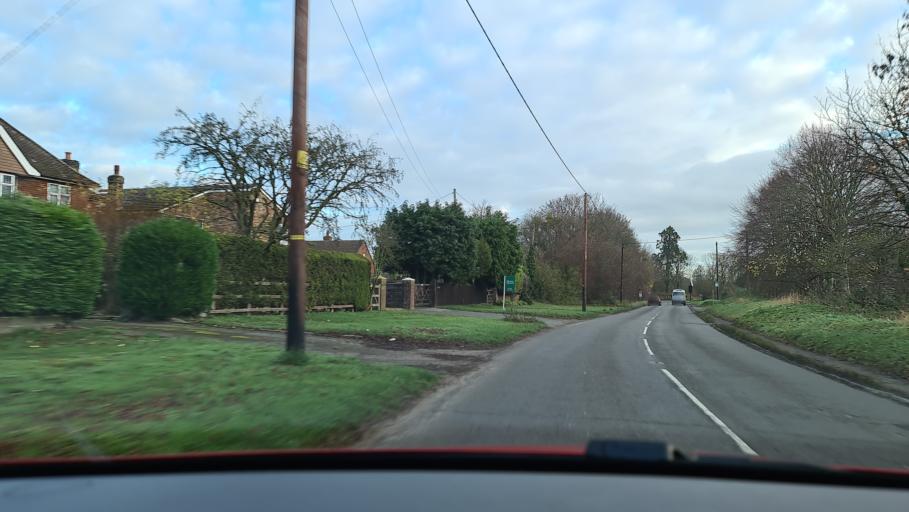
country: GB
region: England
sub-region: Oxfordshire
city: Chinnor
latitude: 51.7196
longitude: -0.8773
